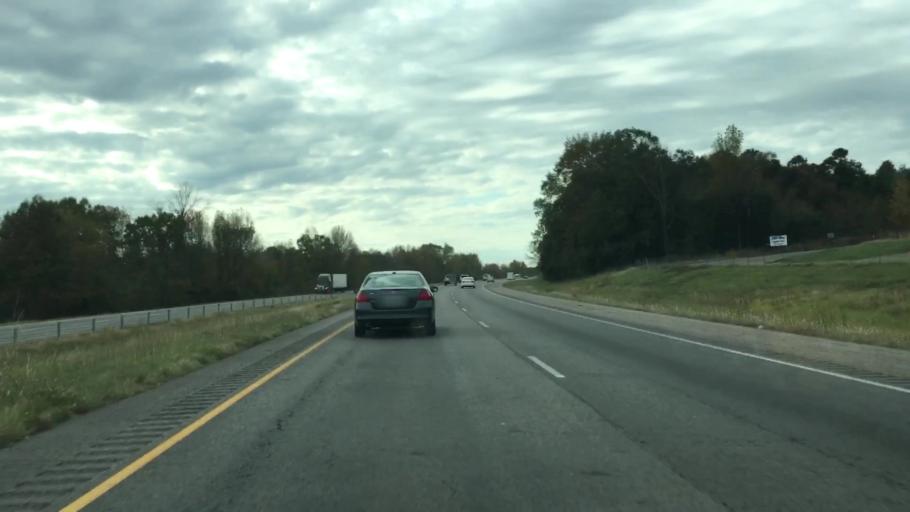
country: US
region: Arkansas
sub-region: Conway County
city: Morrilton
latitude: 35.1629
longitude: -92.6734
